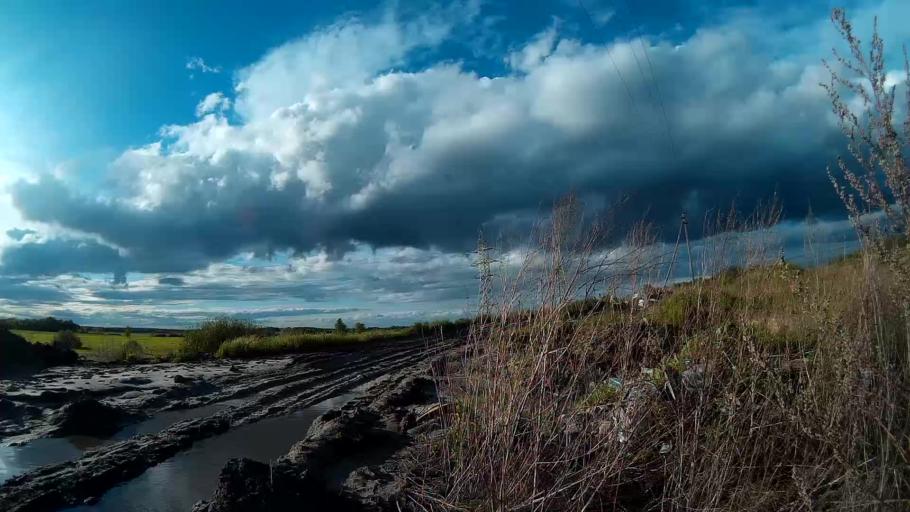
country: RU
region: Ulyanovsk
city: Novoul'yanovsk
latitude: 54.2100
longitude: 48.2766
